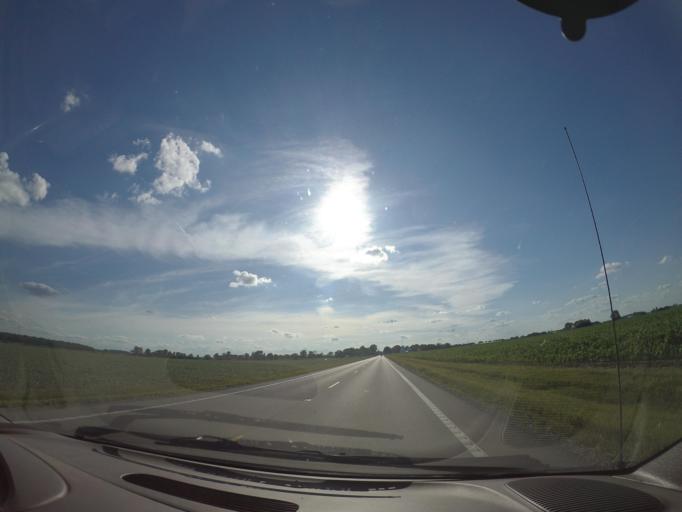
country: US
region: Ohio
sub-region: Henry County
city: Napoleon
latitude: 41.4333
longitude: -84.2291
